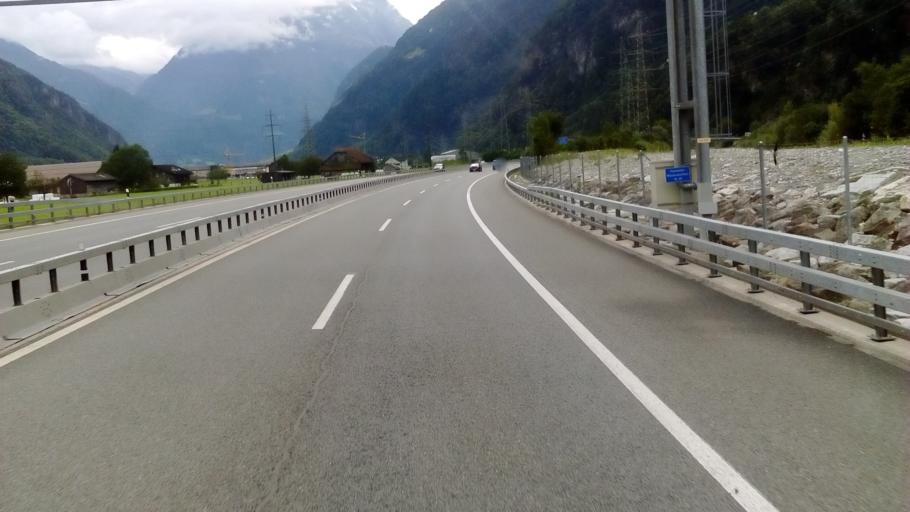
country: CH
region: Uri
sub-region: Uri
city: Attinghausen
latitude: 46.8406
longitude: 8.6366
